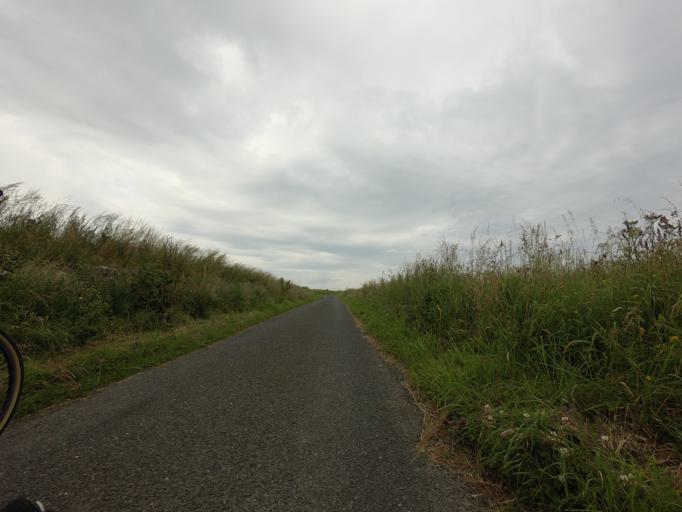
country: GB
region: Scotland
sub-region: Aberdeenshire
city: Whitehills
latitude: 57.6777
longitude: -2.5882
